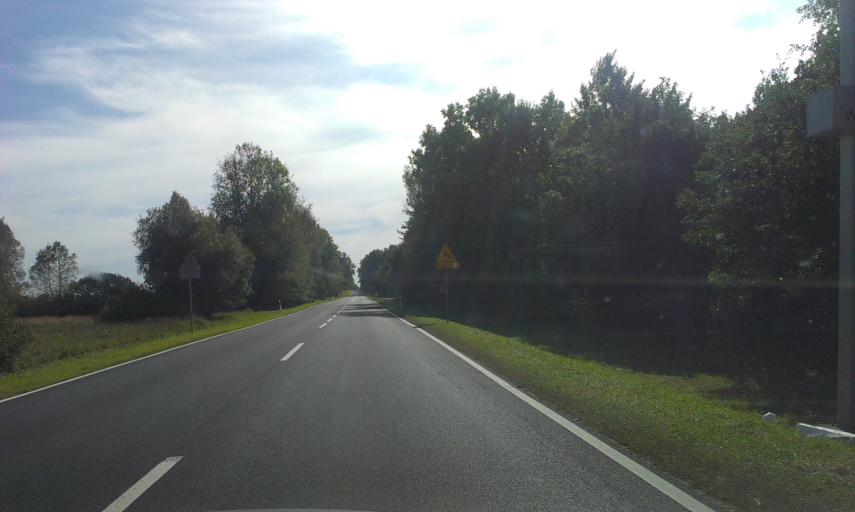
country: PL
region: West Pomeranian Voivodeship
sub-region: Powiat szczecinecki
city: Szczecinek
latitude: 53.6250
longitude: 16.7775
